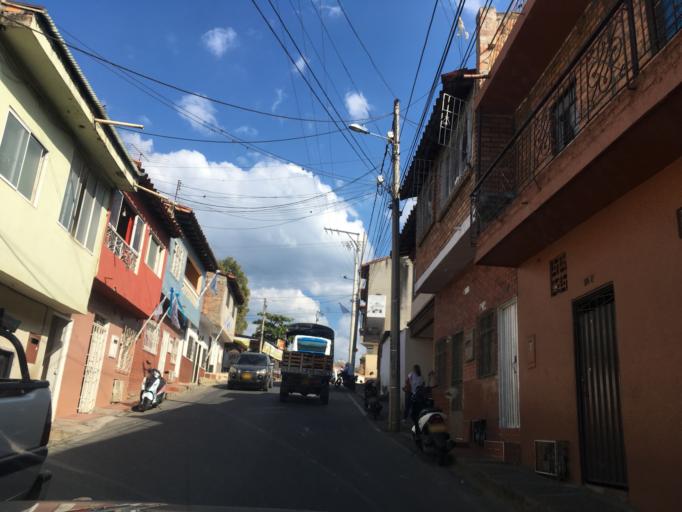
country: CO
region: Santander
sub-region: San Gil
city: San Gil
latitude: 6.5601
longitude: -73.1381
